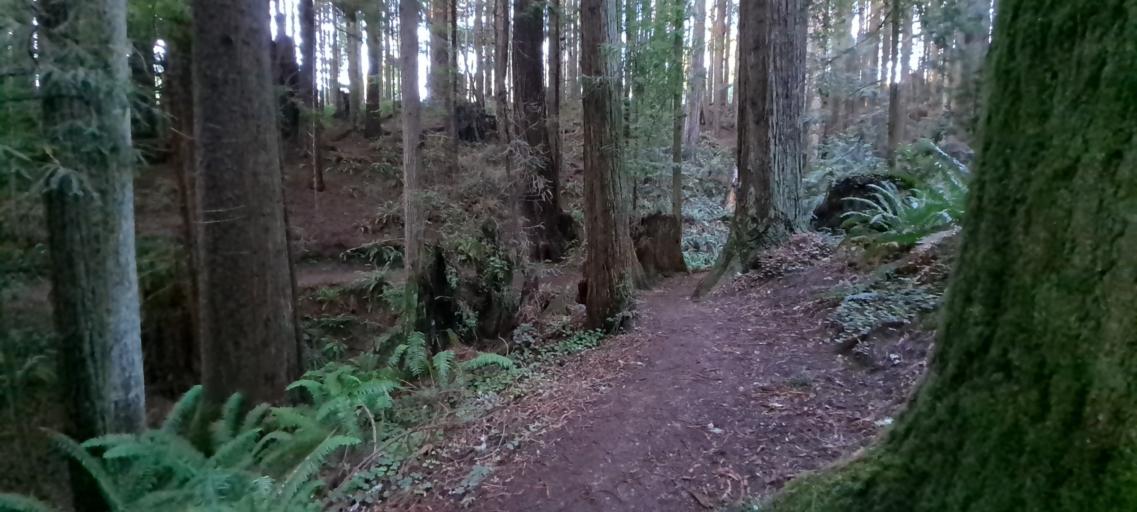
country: US
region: California
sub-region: Humboldt County
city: Arcata
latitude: 40.8715
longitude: -124.0703
